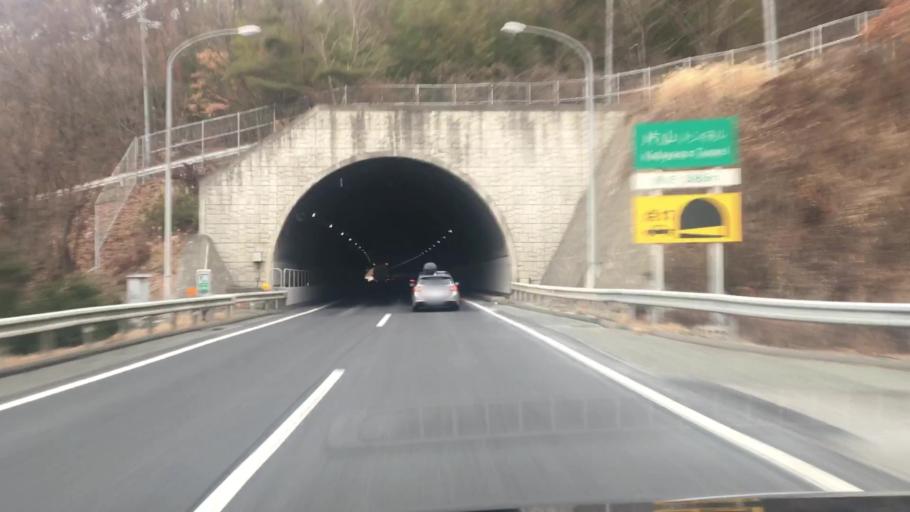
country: JP
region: Nagano
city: Ueda
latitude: 36.4740
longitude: 138.1958
